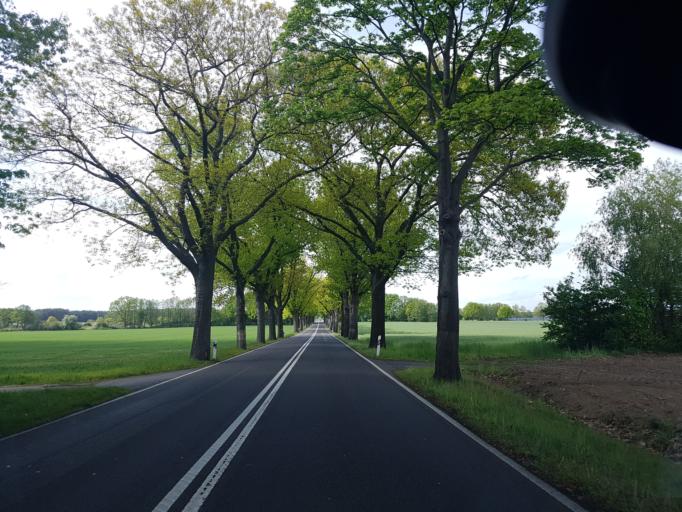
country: DE
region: Saxony
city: Gross Duben
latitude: 51.6744
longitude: 14.5168
